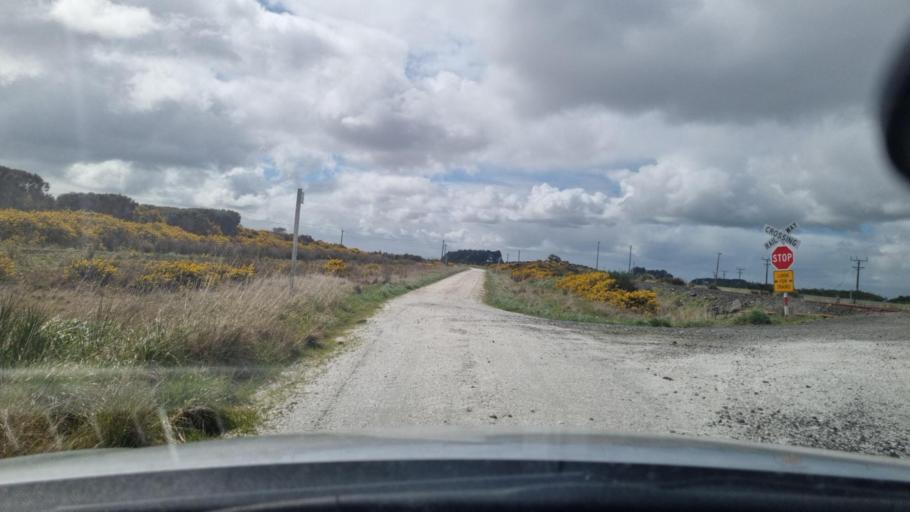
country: NZ
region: Southland
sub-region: Invercargill City
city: Bluff
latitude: -46.5277
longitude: 168.3069
